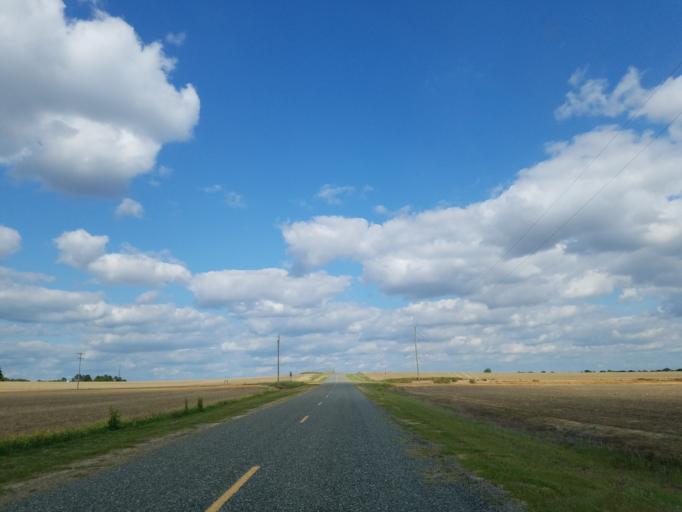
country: US
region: Georgia
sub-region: Dooly County
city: Unadilla
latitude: 32.2364
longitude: -83.7618
